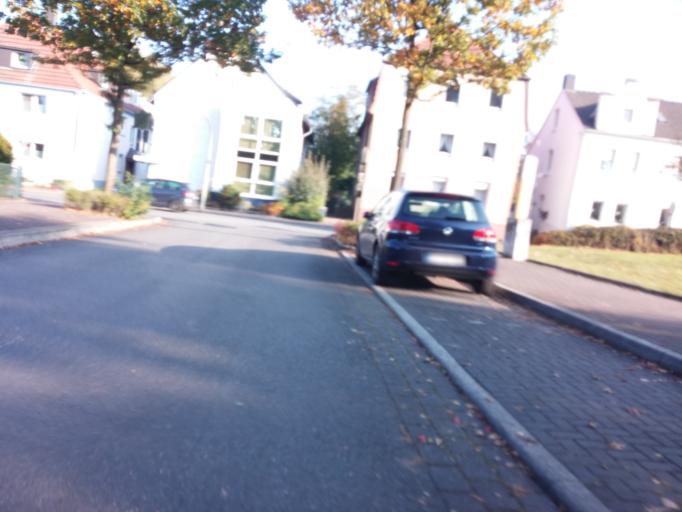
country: DE
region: North Rhine-Westphalia
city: Dorsten
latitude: 51.6576
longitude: 6.9594
